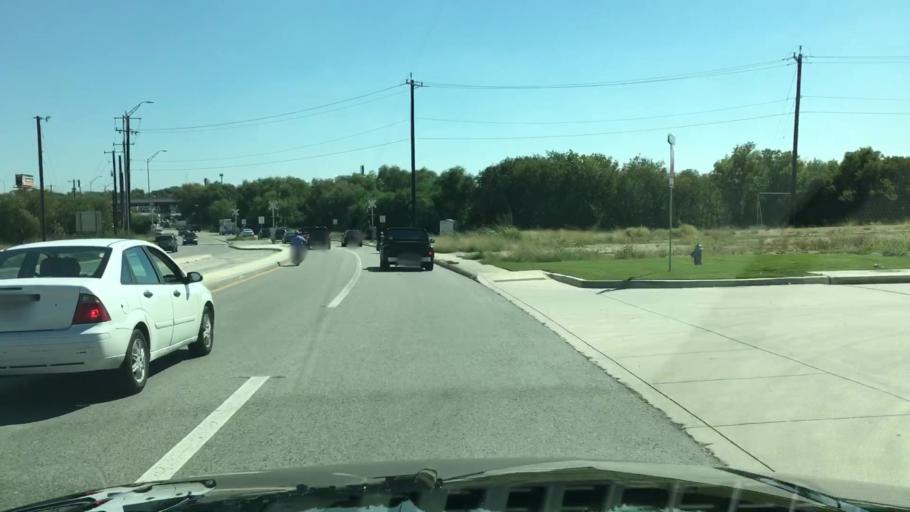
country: US
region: Texas
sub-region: Bexar County
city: Windcrest
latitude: 29.5353
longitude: -98.3936
